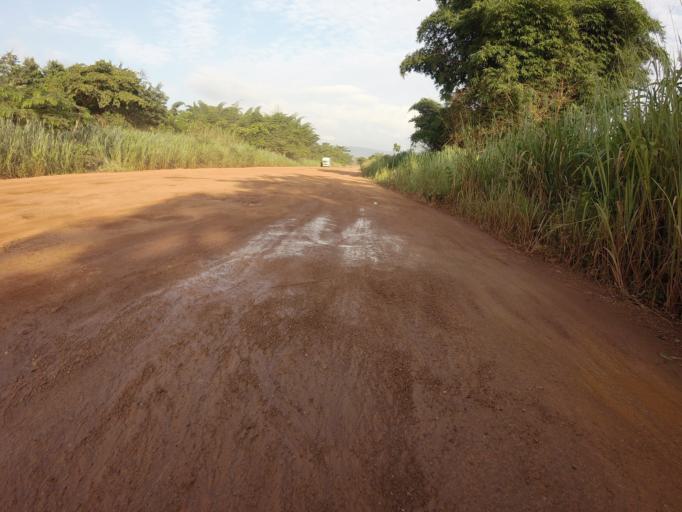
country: GH
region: Volta
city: Kpandu
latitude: 6.9894
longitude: 0.4413
